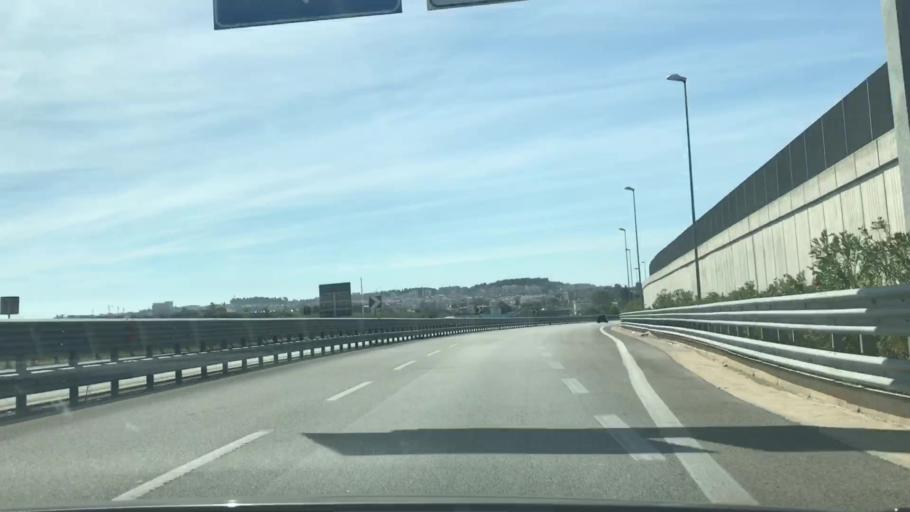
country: IT
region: Basilicate
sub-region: Provincia di Matera
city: Matera
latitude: 40.6927
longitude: 16.5915
